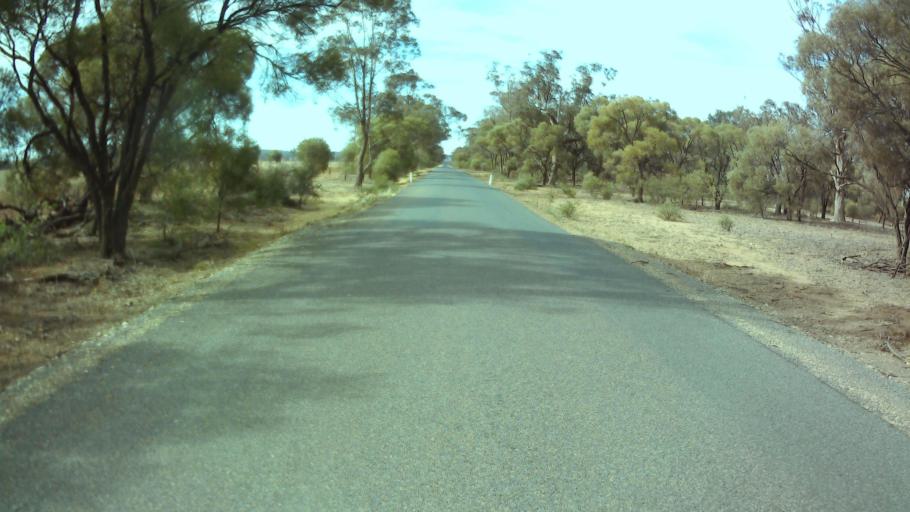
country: AU
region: New South Wales
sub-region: Weddin
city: Grenfell
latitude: -33.8703
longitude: 147.8581
